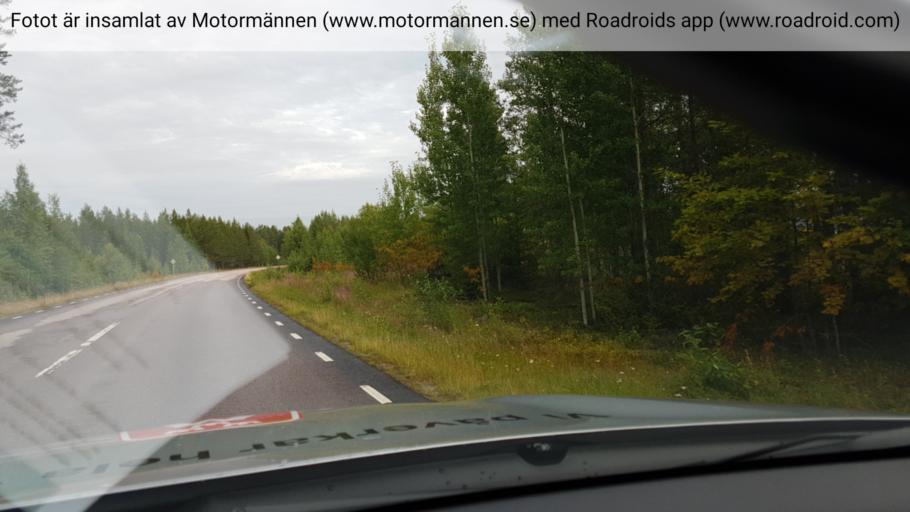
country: SE
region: Norrbotten
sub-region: Lulea Kommun
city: Sodra Sunderbyn
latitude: 65.6278
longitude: 21.9286
